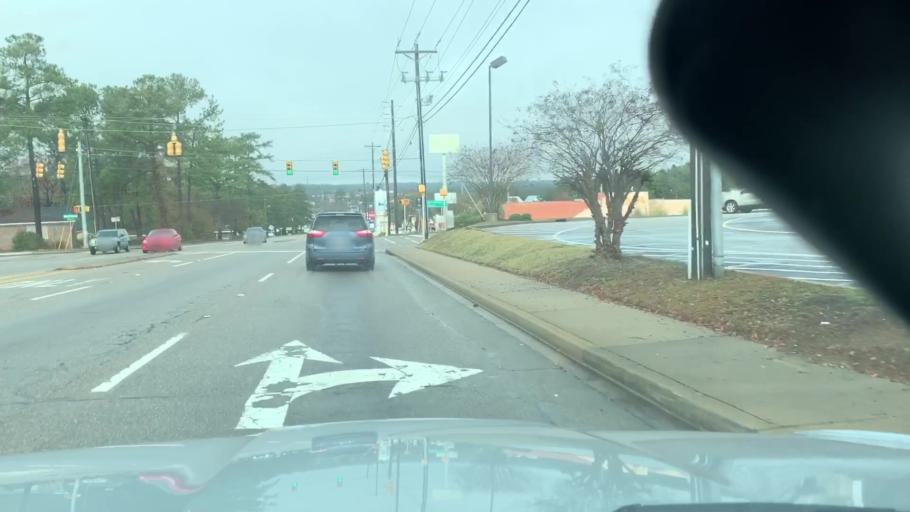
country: US
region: South Carolina
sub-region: Richland County
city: Dentsville
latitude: 34.0534
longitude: -80.9465
